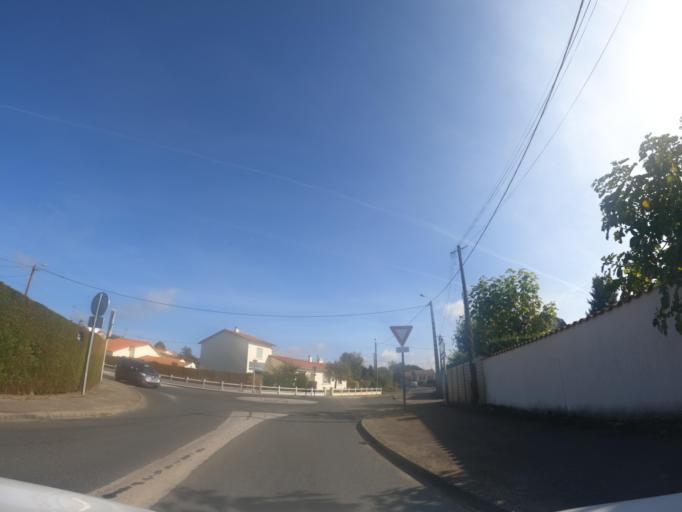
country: FR
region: Poitou-Charentes
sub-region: Departement des Deux-Sevres
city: Courlay
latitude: 46.7802
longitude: -0.5695
